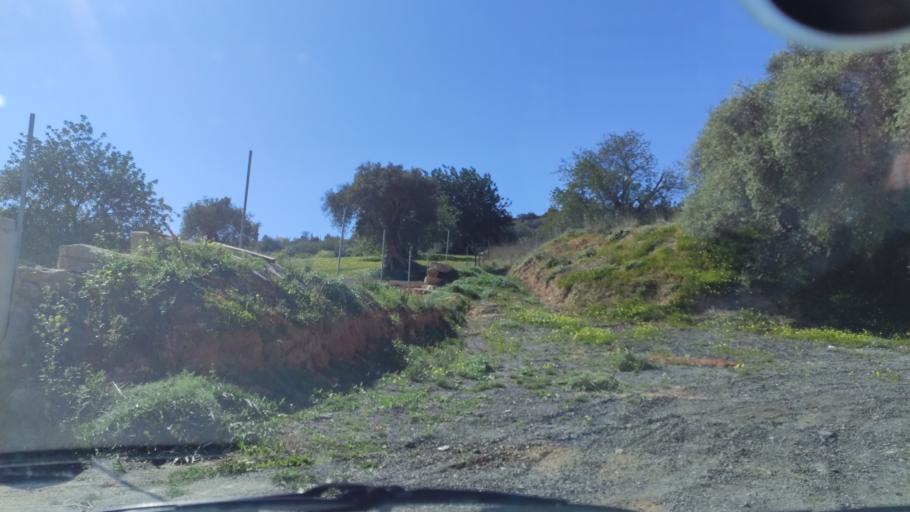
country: PT
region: Faro
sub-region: Sao Bras de Alportel
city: Sao Bras de Alportel
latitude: 37.1141
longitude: -7.9083
